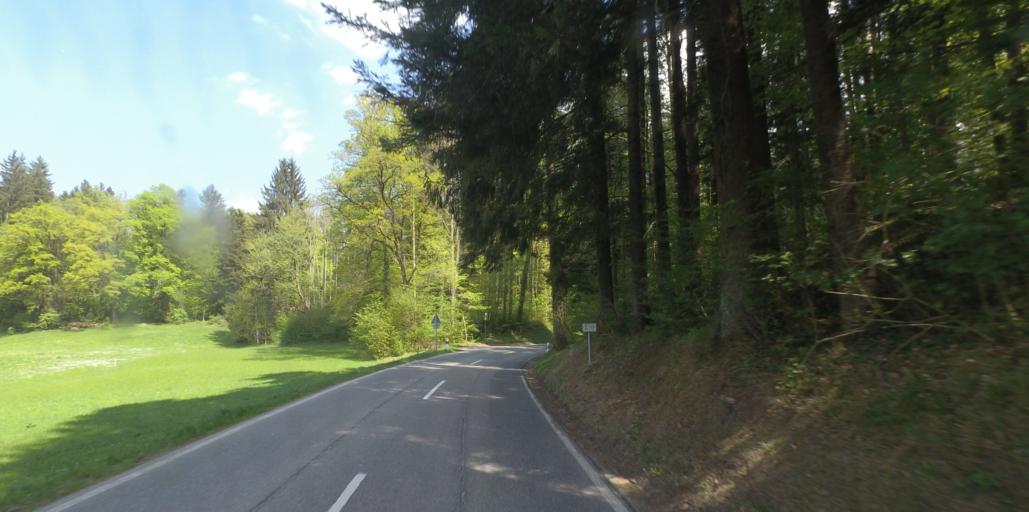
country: DE
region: Bavaria
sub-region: Upper Bavaria
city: Marquartstein
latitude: 47.7460
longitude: 12.4519
